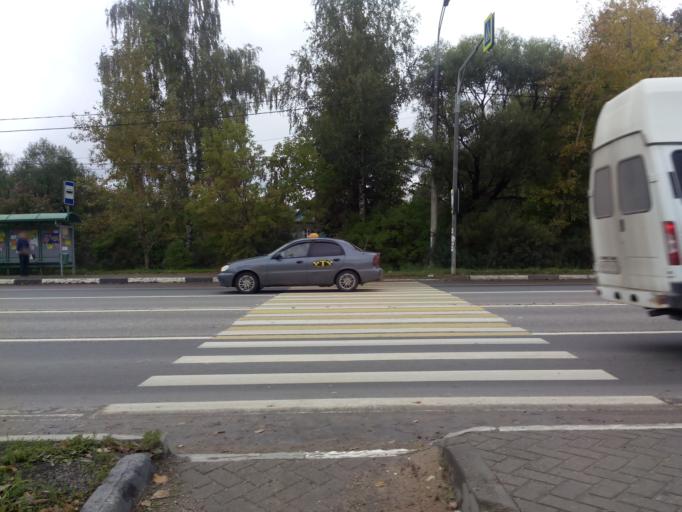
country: RU
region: Moskovskaya
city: Golitsyno
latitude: 55.6297
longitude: 37.0111
